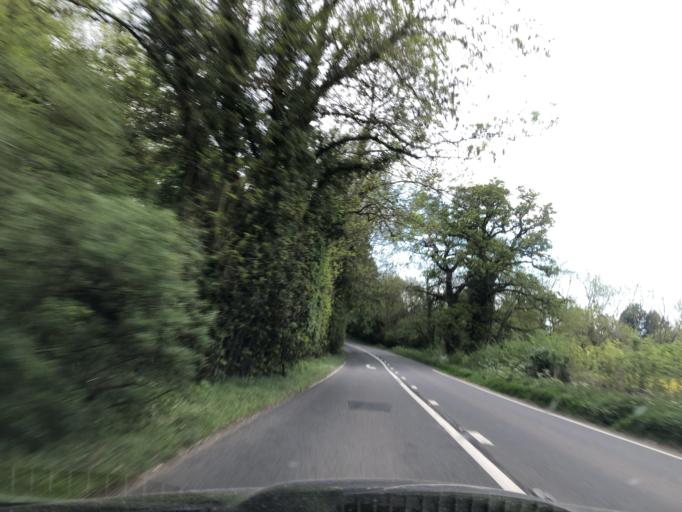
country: GB
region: England
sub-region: Gloucestershire
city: Donnington
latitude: 51.9578
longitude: -1.7129
